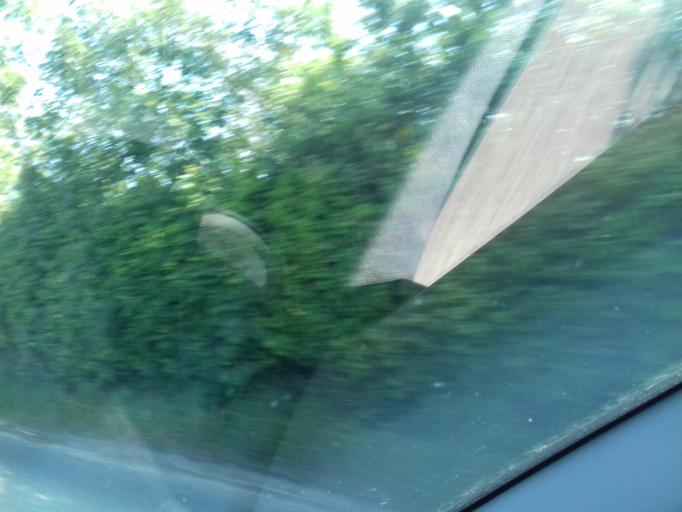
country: IE
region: Leinster
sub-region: An Mhi
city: Stamullin
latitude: 53.5978
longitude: -6.2449
